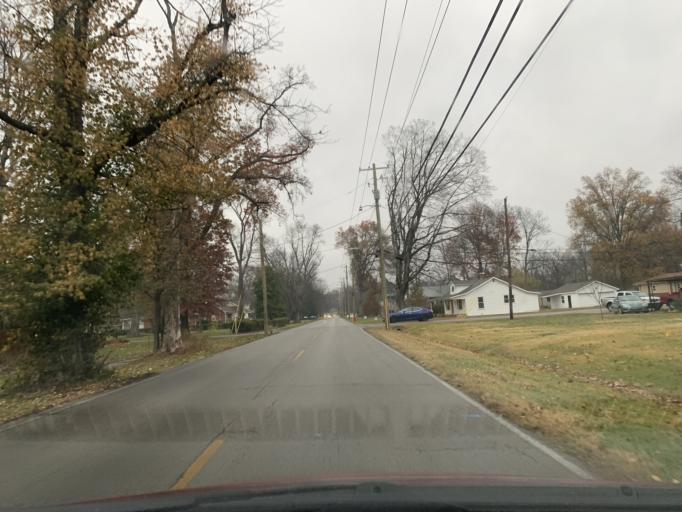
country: US
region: Kentucky
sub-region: Jefferson County
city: Buechel
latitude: 38.1970
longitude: -85.6483
